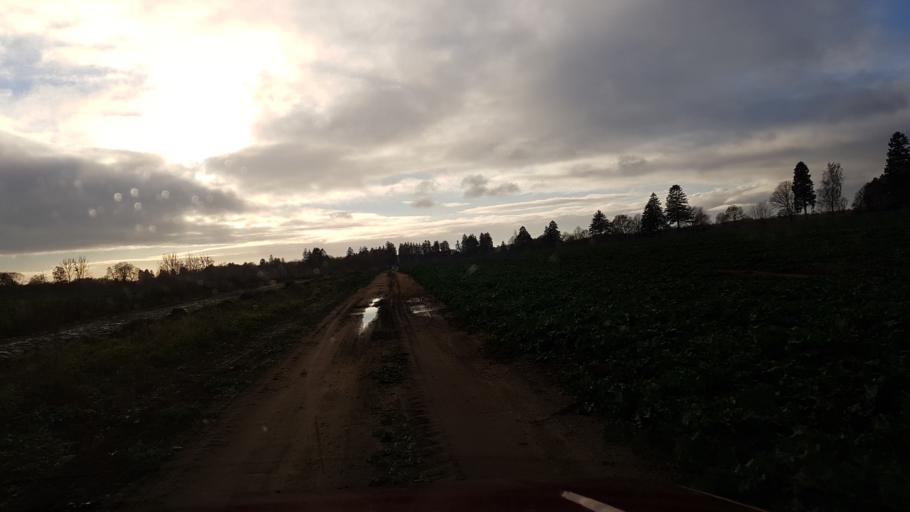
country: PL
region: West Pomeranian Voivodeship
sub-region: Powiat szczecinecki
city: Grzmiaca
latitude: 53.9875
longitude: 16.4032
